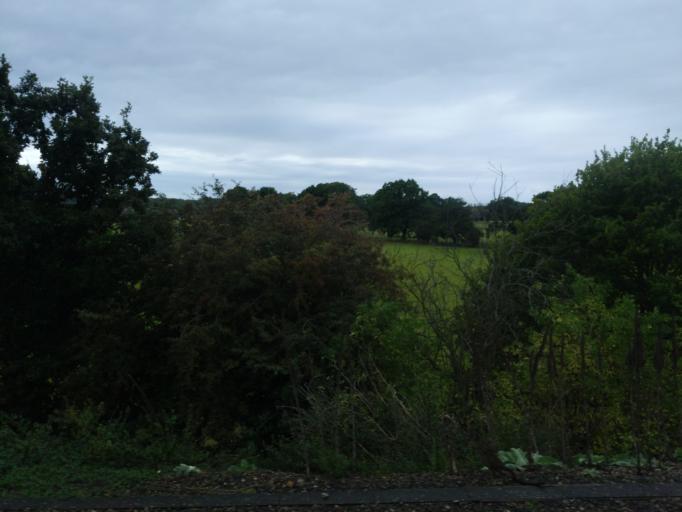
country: GB
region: England
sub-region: Kent
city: Tonbridge
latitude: 51.2057
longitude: 0.2494
